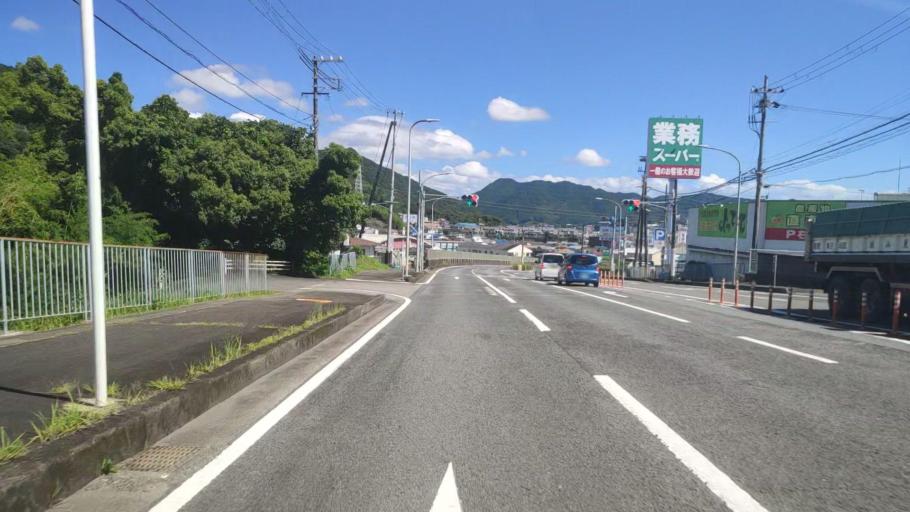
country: JP
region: Wakayama
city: Shingu
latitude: 33.7094
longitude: 135.9877
